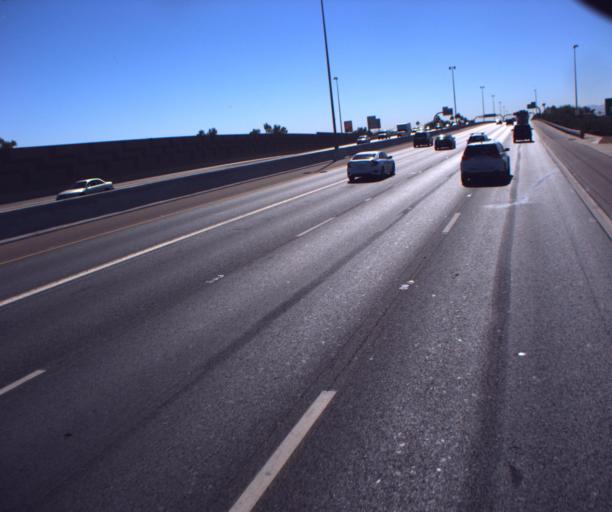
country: US
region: Arizona
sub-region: Maricopa County
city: Sun City
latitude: 33.5845
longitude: -112.2605
